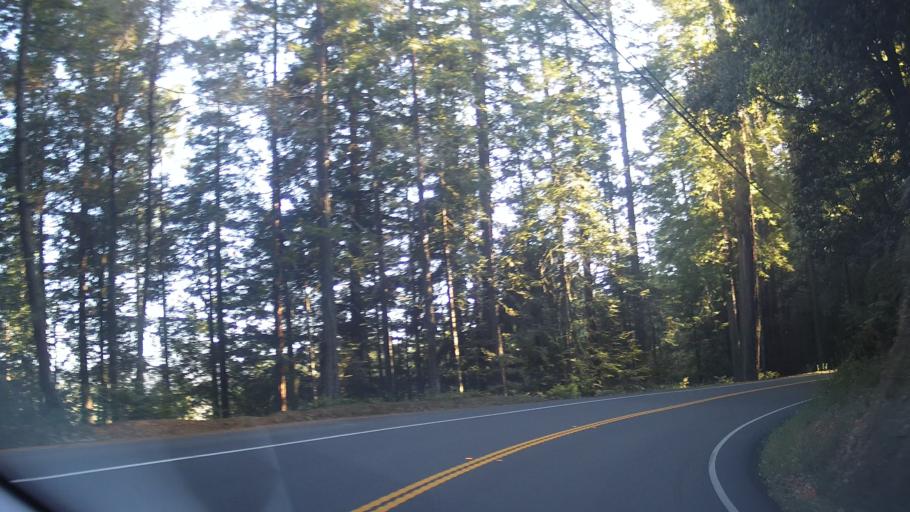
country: US
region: California
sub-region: Mendocino County
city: Fort Bragg
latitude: 39.4051
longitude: -123.7340
